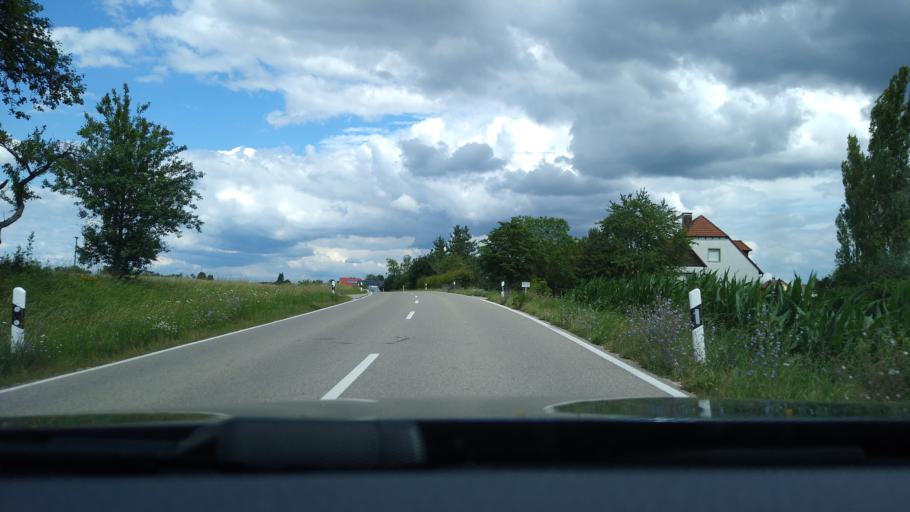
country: DE
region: Bavaria
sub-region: Regierungsbezirk Mittelfranken
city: Haundorf
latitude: 49.1507
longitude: 10.8008
